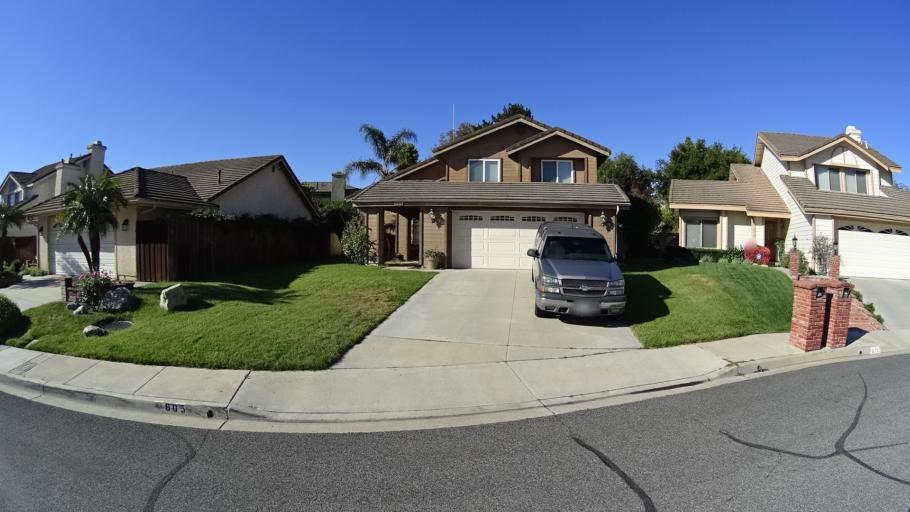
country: US
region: California
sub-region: Ventura County
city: Casa Conejo
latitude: 34.1889
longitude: -118.9107
